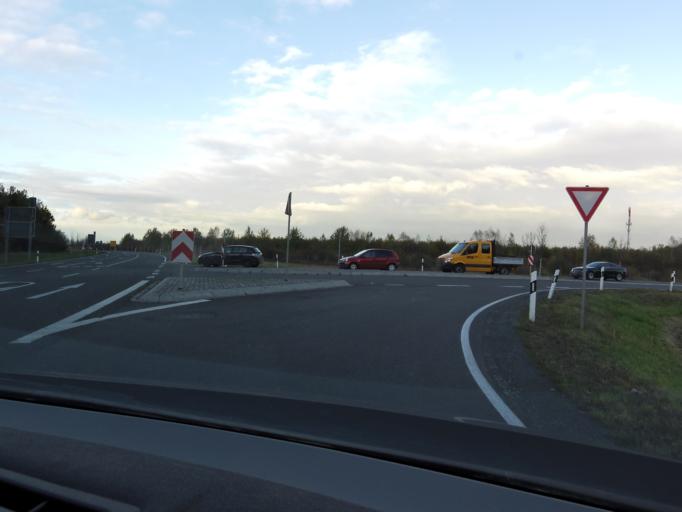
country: DE
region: Saxony
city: Zwochau
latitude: 51.4196
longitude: 12.2850
